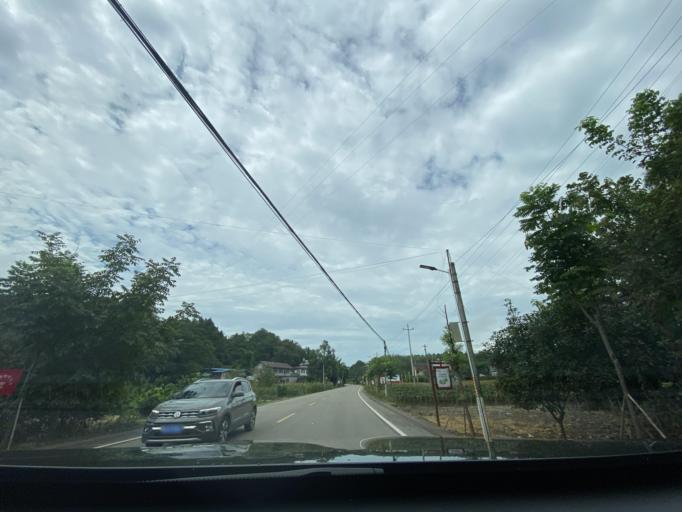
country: CN
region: Sichuan
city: Jiancheng
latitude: 30.4780
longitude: 104.6307
